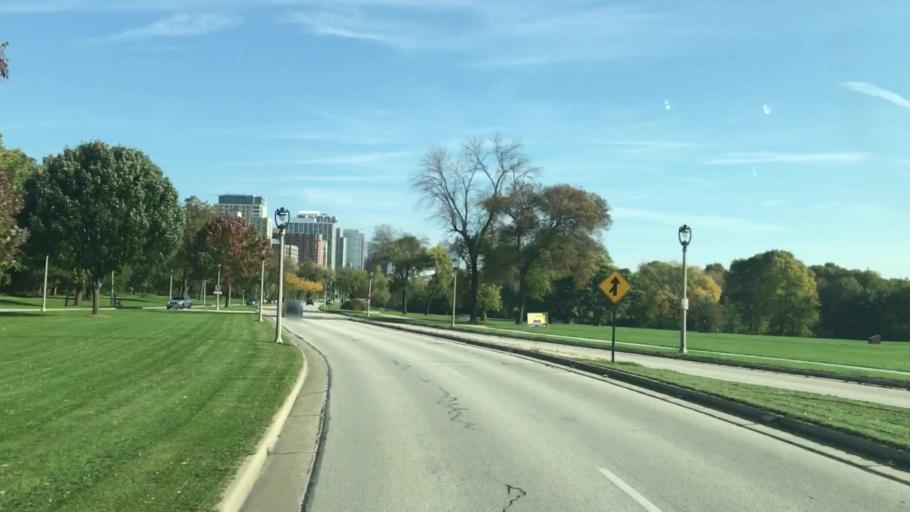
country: US
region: Wisconsin
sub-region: Milwaukee County
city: Milwaukee
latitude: 43.0432
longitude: -87.8966
